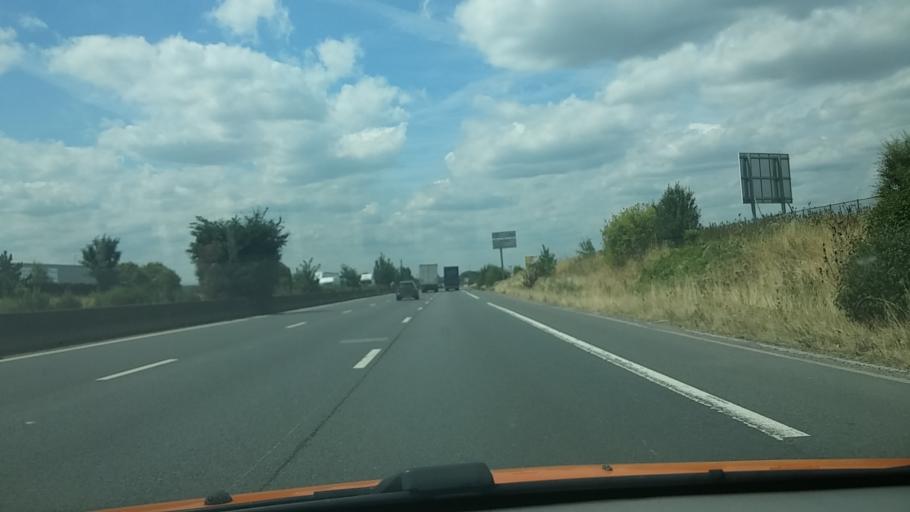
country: FR
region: Ile-de-France
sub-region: Departement de Seine-Saint-Denis
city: Tremblay-en-France
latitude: 48.9686
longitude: 2.5655
